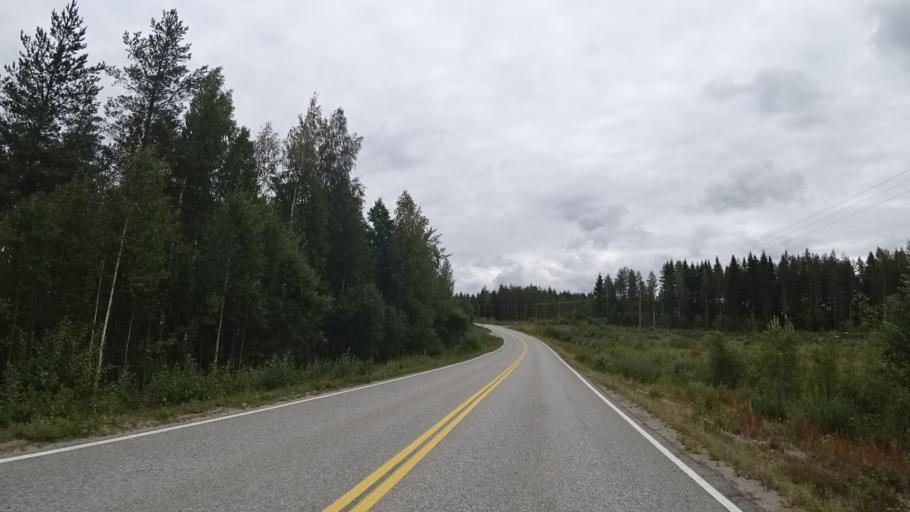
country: FI
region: North Karelia
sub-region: Joensuu
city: Ilomantsi
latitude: 62.6247
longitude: 31.2482
